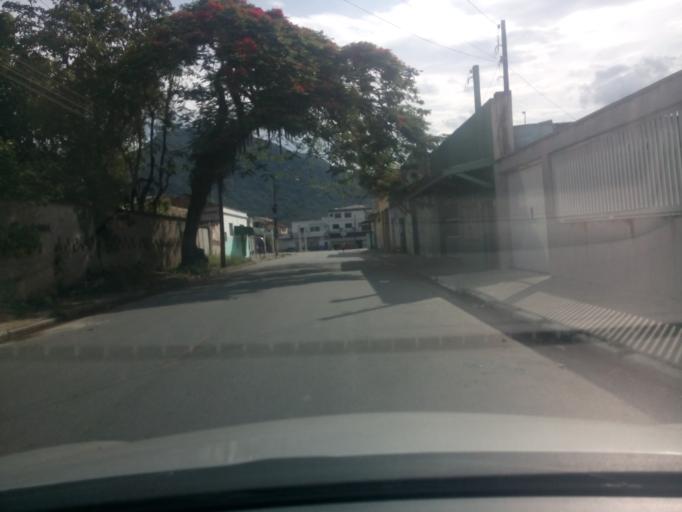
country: BR
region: Sao Paulo
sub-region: Peruibe
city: Peruibe
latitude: -24.3210
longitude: -47.0016
